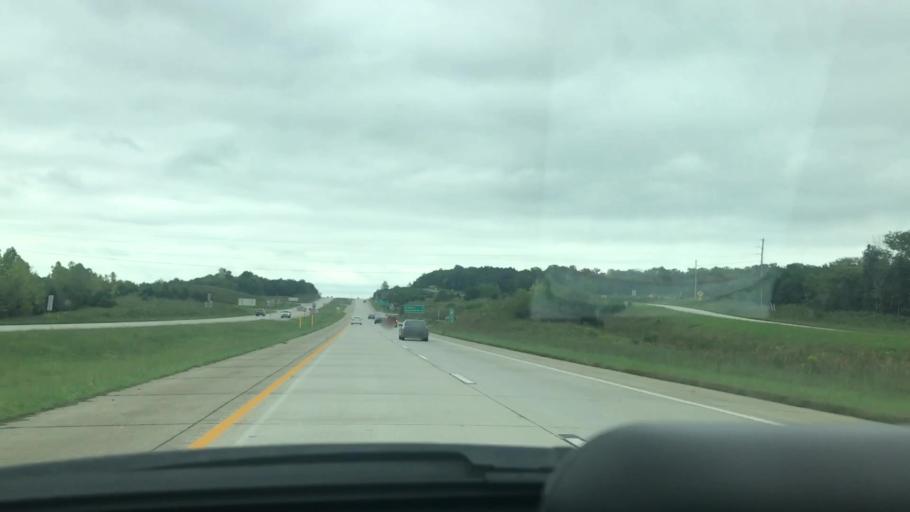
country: US
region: Missouri
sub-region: Greene County
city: Fair Grove
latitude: 37.5141
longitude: -93.1385
